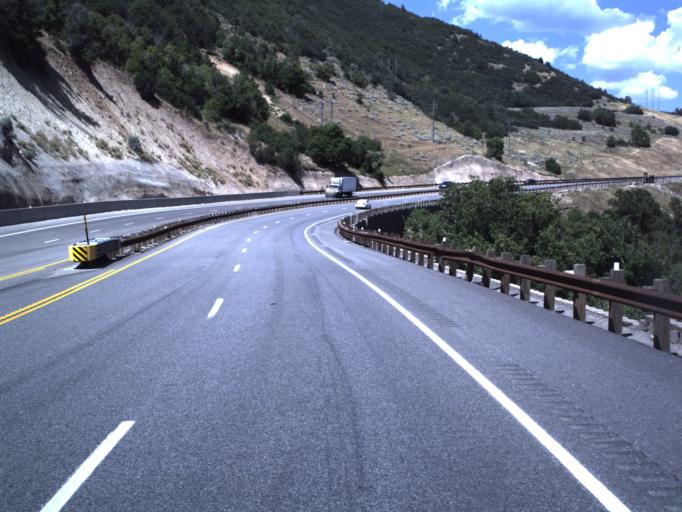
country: US
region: Utah
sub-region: Wasatch County
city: Midway
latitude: 40.3825
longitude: -111.5515
